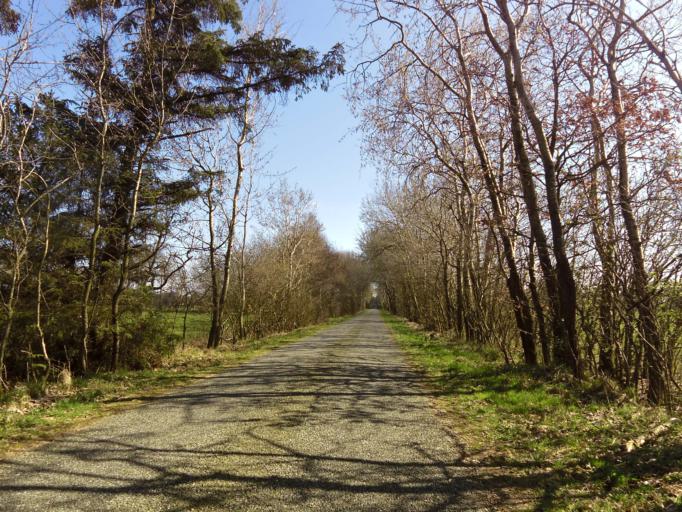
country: DK
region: South Denmark
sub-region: Esbjerg Kommune
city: Ribe
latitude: 55.3453
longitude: 8.8472
